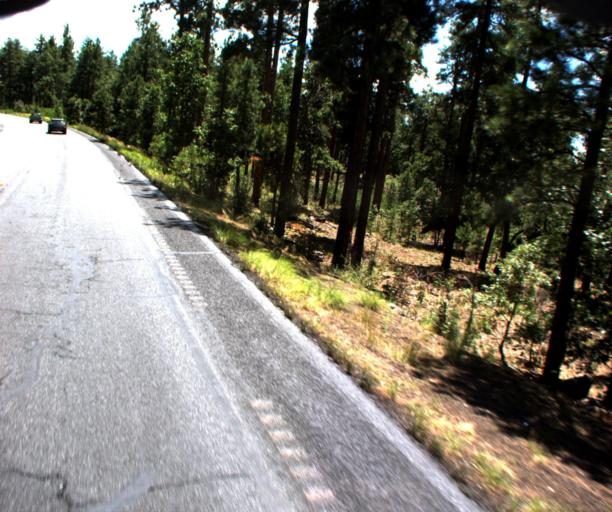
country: US
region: Arizona
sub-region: Gila County
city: Pine
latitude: 34.4681
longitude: -111.4478
